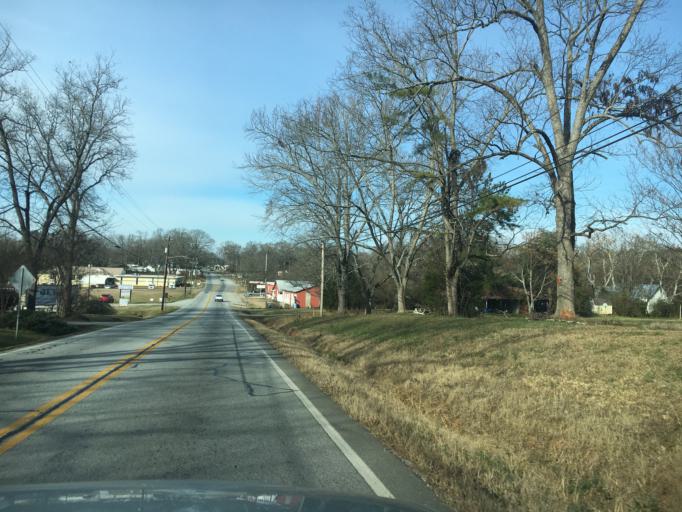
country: US
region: Georgia
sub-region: Jackson County
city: Hoschton
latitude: 34.0902
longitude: -83.7587
